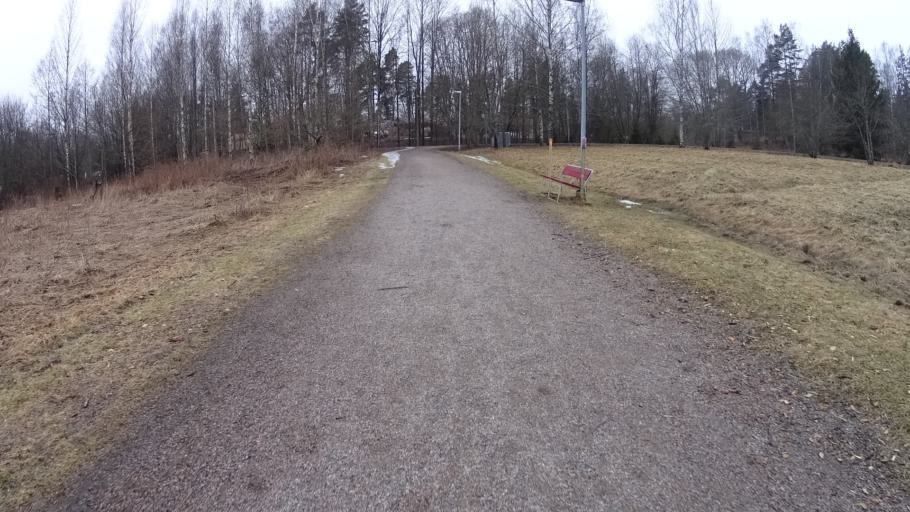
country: FI
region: Uusimaa
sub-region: Helsinki
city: Kilo
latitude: 60.2624
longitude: 24.7945
